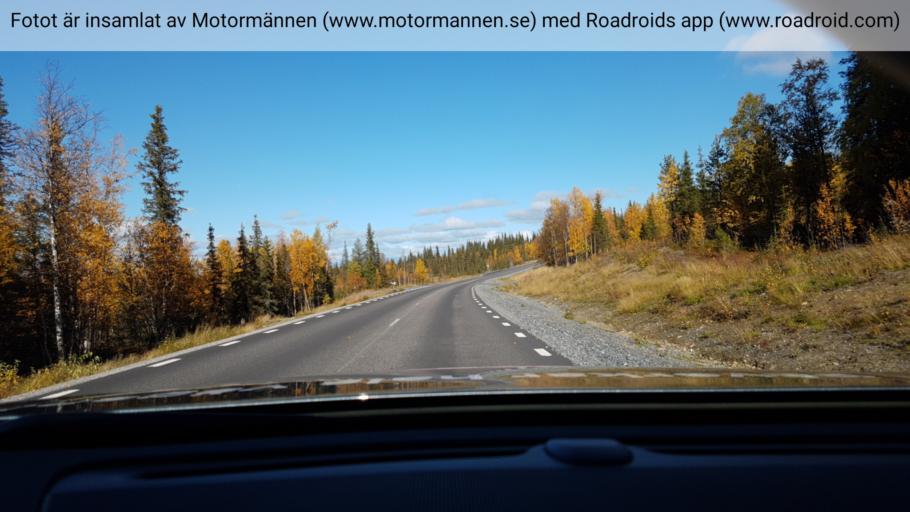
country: SE
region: Norrbotten
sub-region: Gallivare Kommun
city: Gaellivare
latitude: 67.0326
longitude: 20.7275
